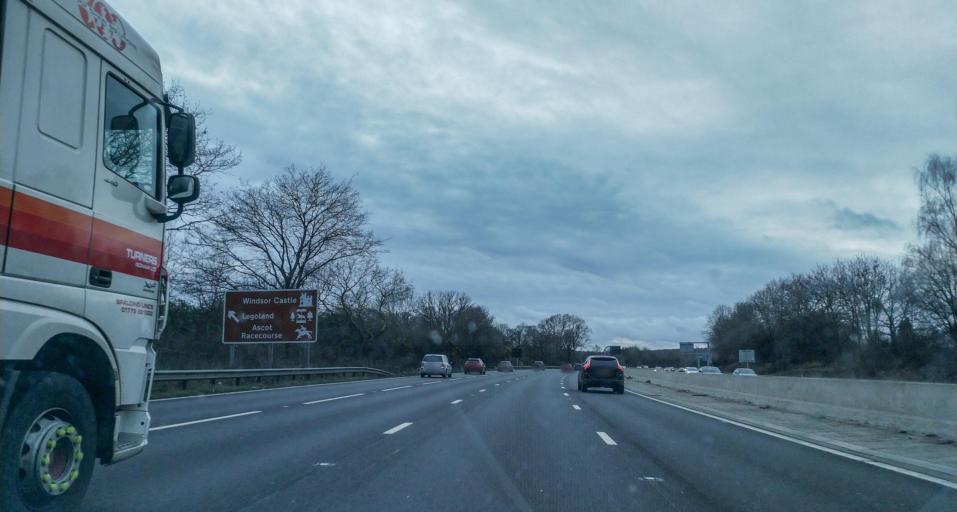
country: GB
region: England
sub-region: Surrey
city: Windlesham
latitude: 51.3601
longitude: -0.6513
